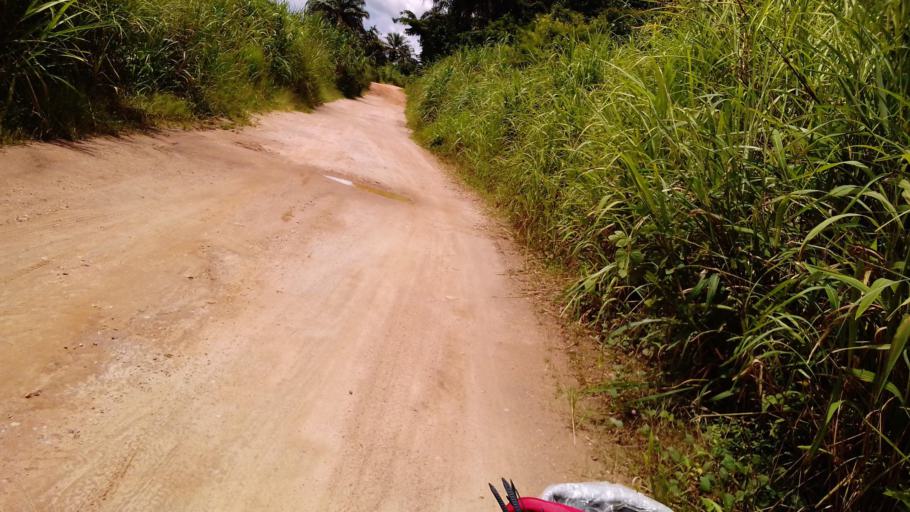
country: SL
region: Eastern Province
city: Koyima
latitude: 8.6916
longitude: -11.0093
